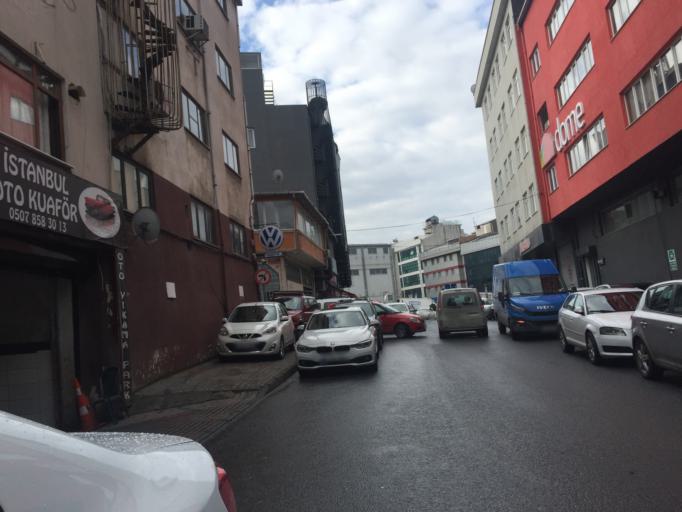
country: TR
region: Istanbul
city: Sisli
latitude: 41.0935
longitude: 29.0030
